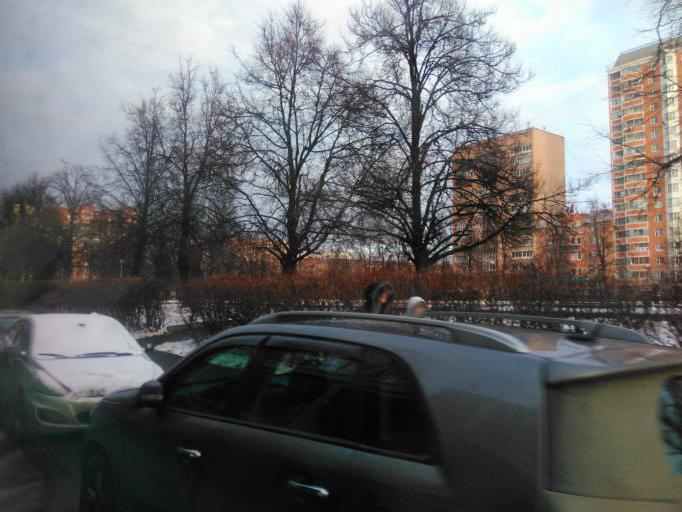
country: RU
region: Moscow
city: Nagornyy
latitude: 55.6521
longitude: 37.6115
